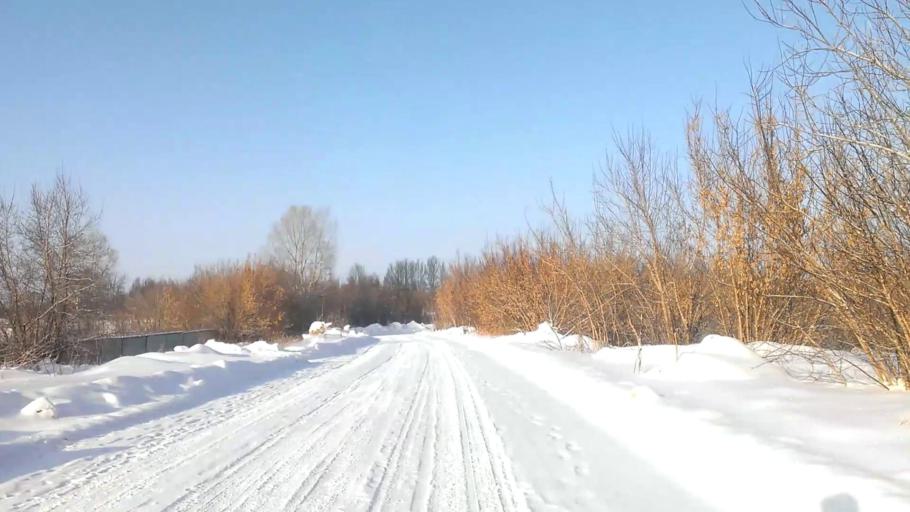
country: RU
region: Altai Krai
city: Novosilikatnyy
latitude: 53.3452
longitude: 83.6299
